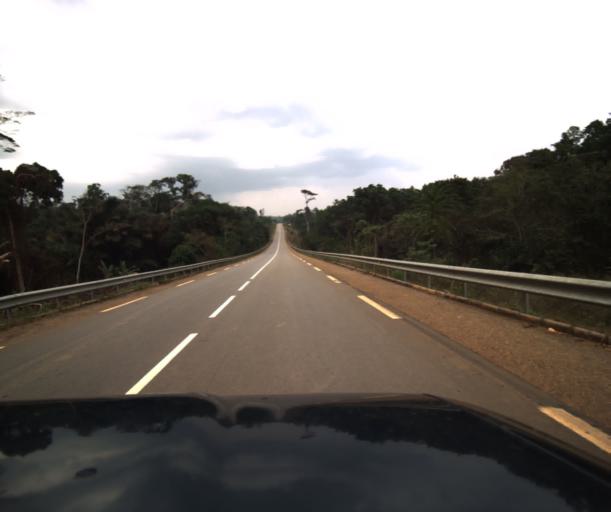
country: CM
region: Centre
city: Akono
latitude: 3.6331
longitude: 11.3248
